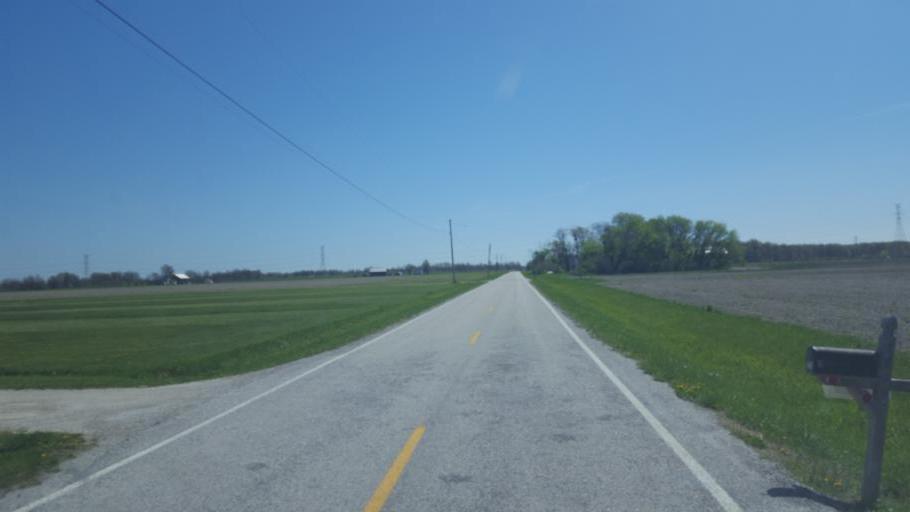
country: US
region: Ohio
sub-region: Ottawa County
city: Oak Harbor
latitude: 41.4972
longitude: -83.0812
